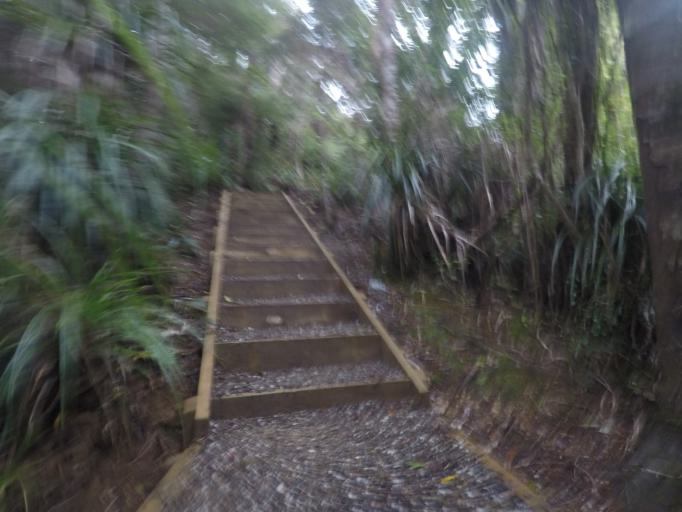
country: NZ
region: Auckland
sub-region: Auckland
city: Titirangi
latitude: -37.0013
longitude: 174.5352
